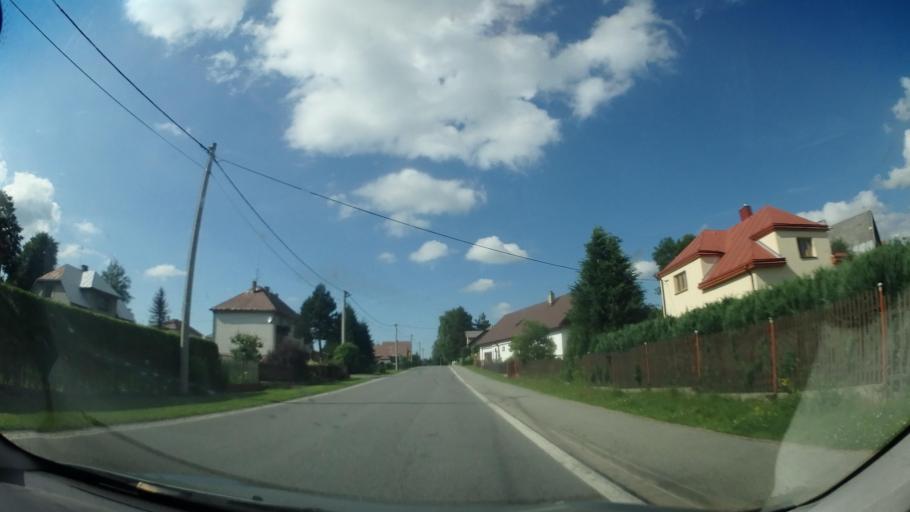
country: CZ
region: Vysocina
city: Heralec
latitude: 49.6931
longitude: 15.9930
